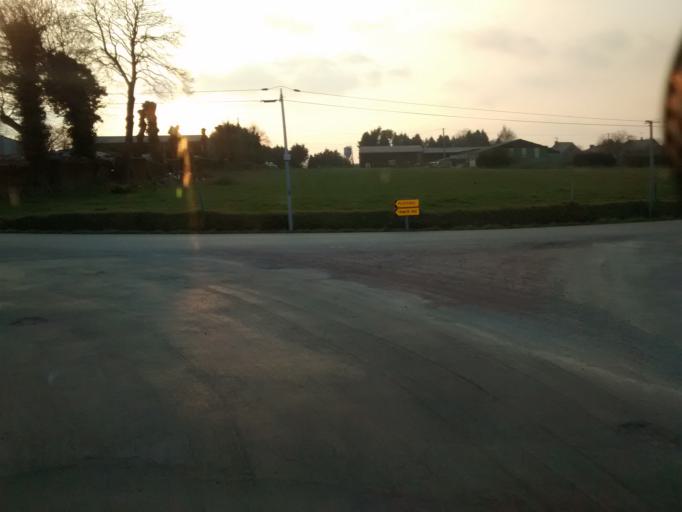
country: FR
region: Brittany
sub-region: Departement du Morbihan
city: Meneac
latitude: 48.1429
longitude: -2.4641
